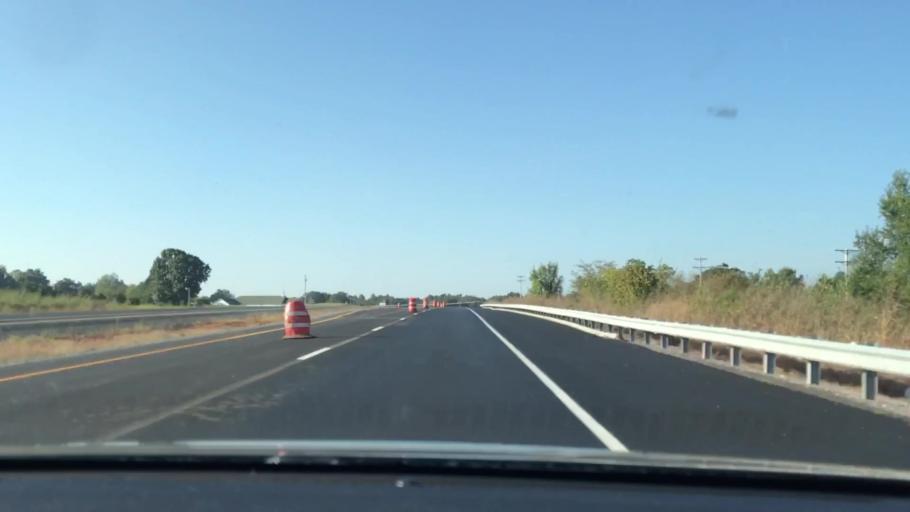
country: US
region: Kentucky
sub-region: Trigg County
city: Cadiz
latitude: 36.8481
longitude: -87.8211
